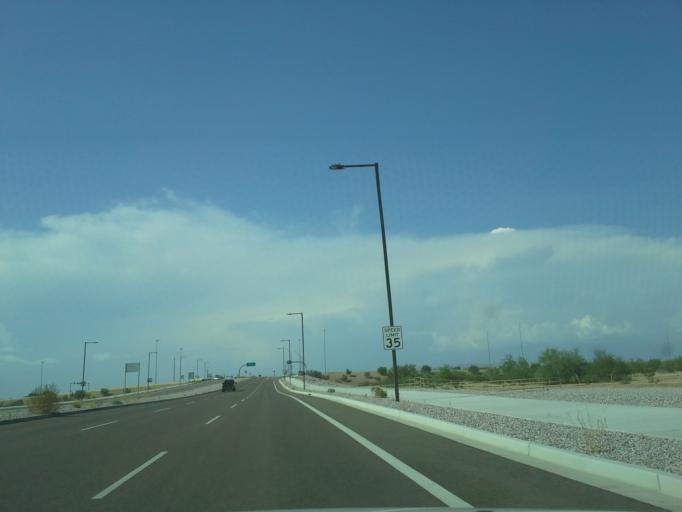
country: US
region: Arizona
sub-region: Maricopa County
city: Paradise Valley
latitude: 33.6574
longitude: -111.9426
